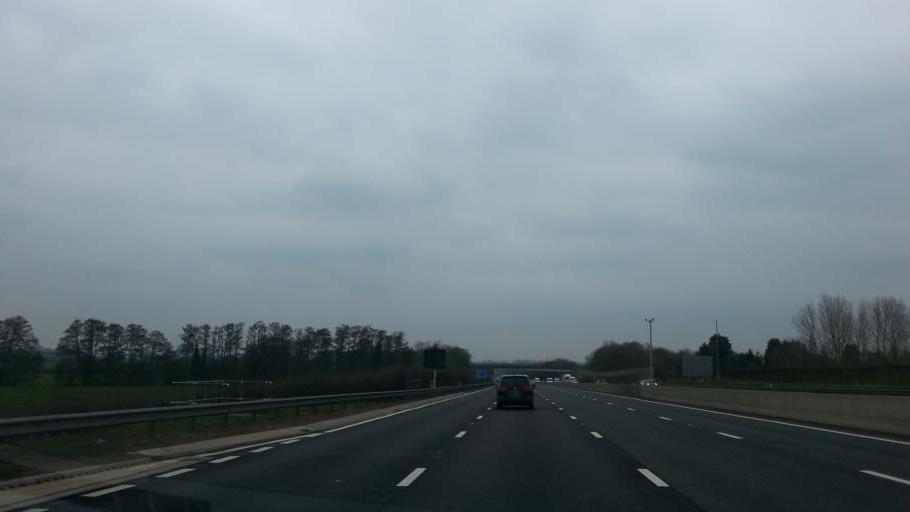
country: GB
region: England
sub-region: Worcestershire
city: Droitwich
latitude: 52.3036
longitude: -2.1100
